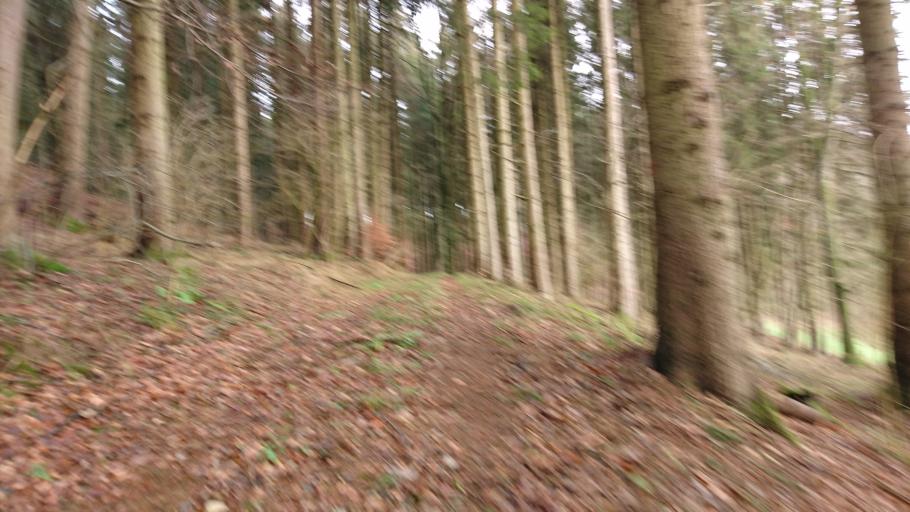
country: DE
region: Bavaria
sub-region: Swabia
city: Zusmarshausen
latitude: 48.4307
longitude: 10.6068
